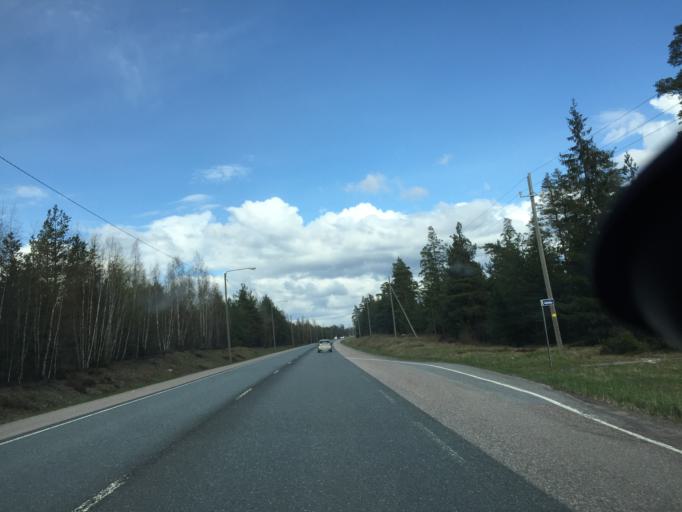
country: FI
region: Uusimaa
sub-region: Raaseporin
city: Ekenaes
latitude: 59.9993
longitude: 23.5142
